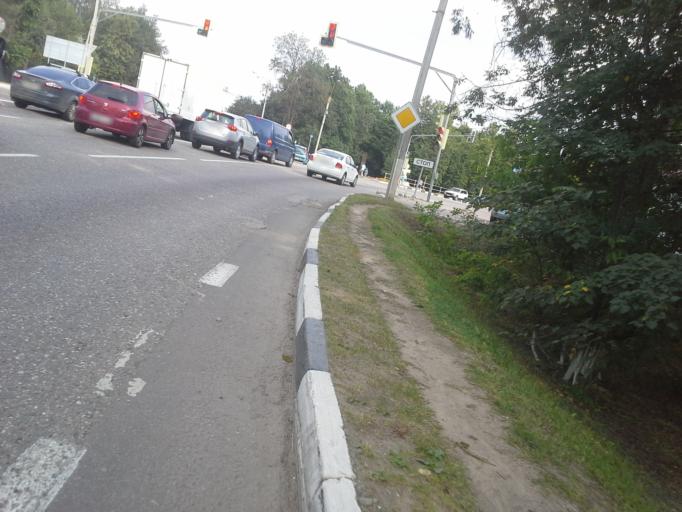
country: RU
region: Moskovskaya
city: Istra
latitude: 55.9205
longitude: 36.8571
